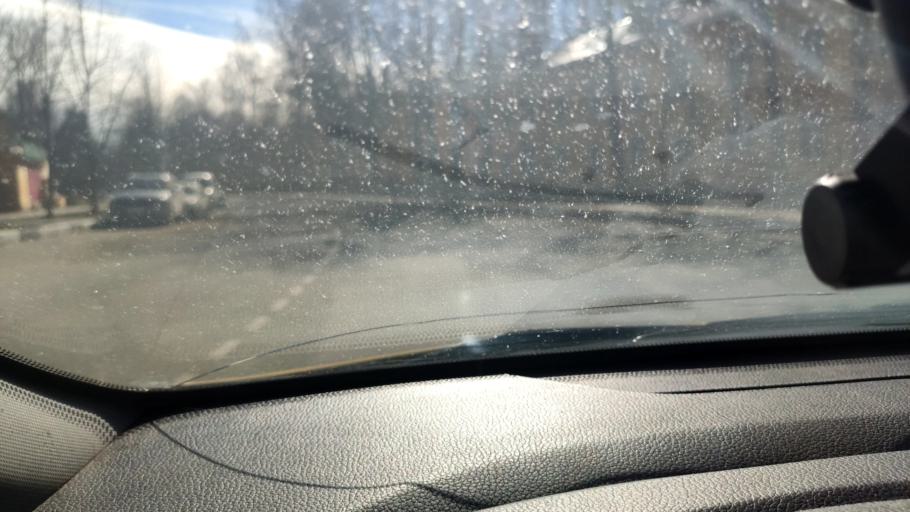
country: RU
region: Moskovskaya
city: Selyatino
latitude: 55.5147
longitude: 36.9718
